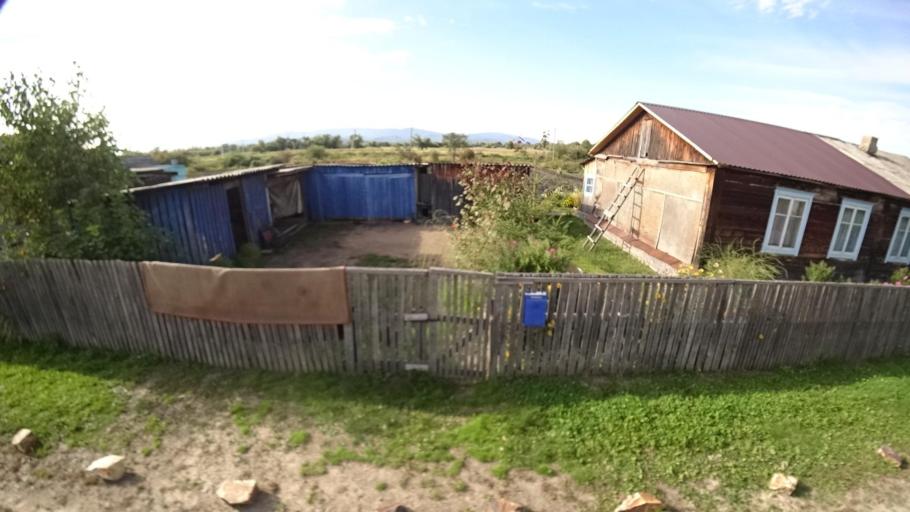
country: RU
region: Primorskiy
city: Dostoyevka
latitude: 44.3079
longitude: 133.4640
